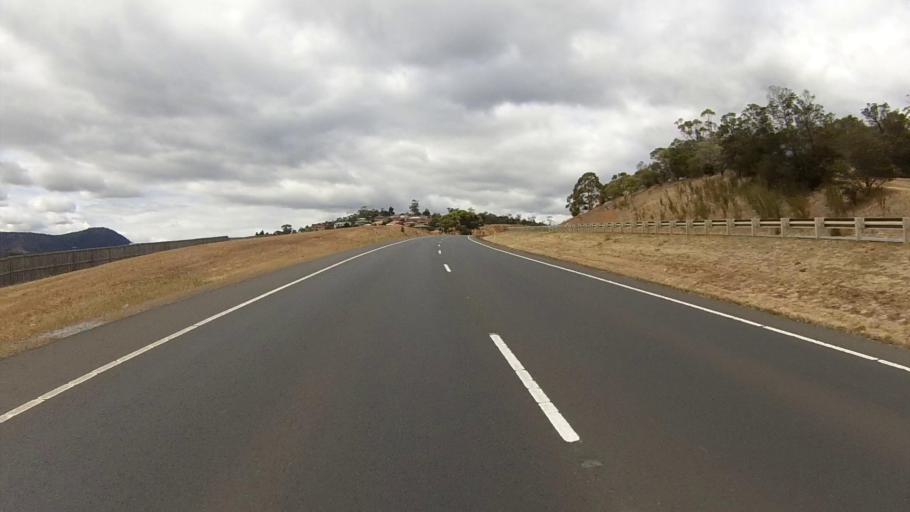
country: AU
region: Tasmania
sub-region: Glenorchy
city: Austins Ferry
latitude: -42.7702
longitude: 147.2376
